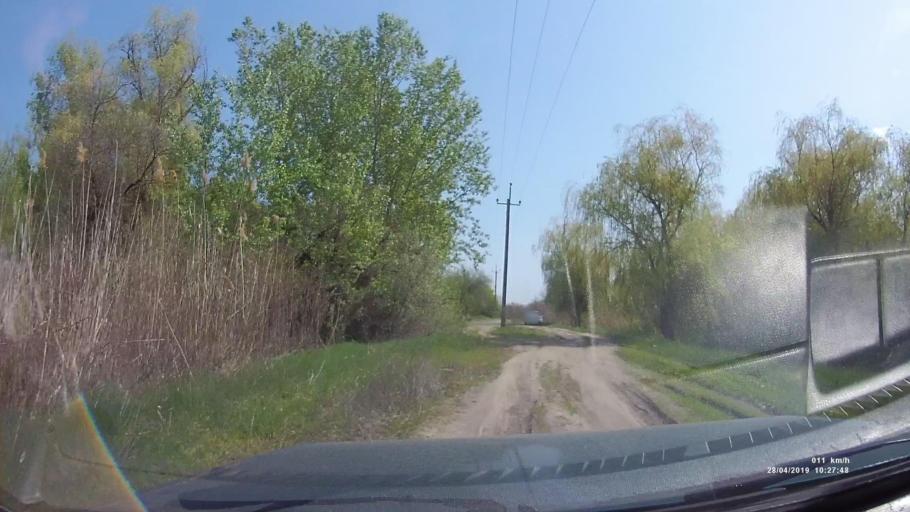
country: RU
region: Rostov
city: Azov
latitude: 47.1152
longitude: 39.4470
